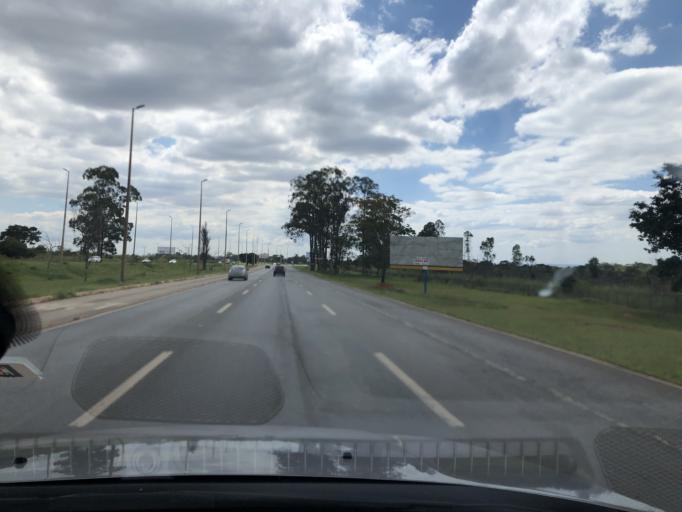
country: BR
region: Federal District
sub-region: Brasilia
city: Brasilia
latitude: -15.9571
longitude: -47.9937
